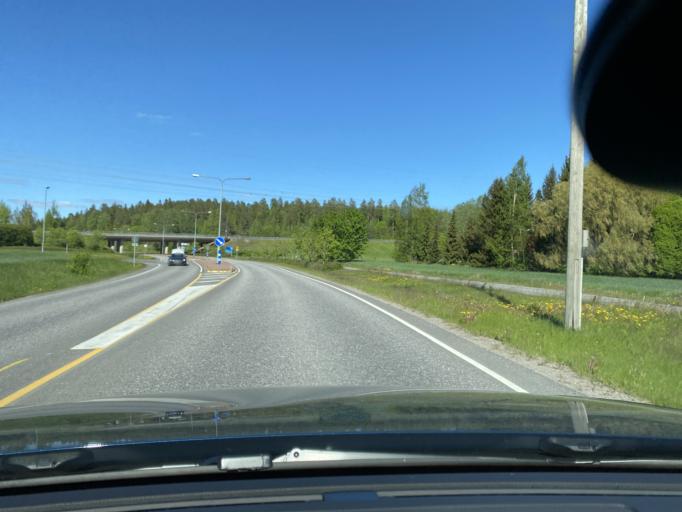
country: FI
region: Varsinais-Suomi
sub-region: Turku
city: Paimio
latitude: 60.4234
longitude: 22.6693
